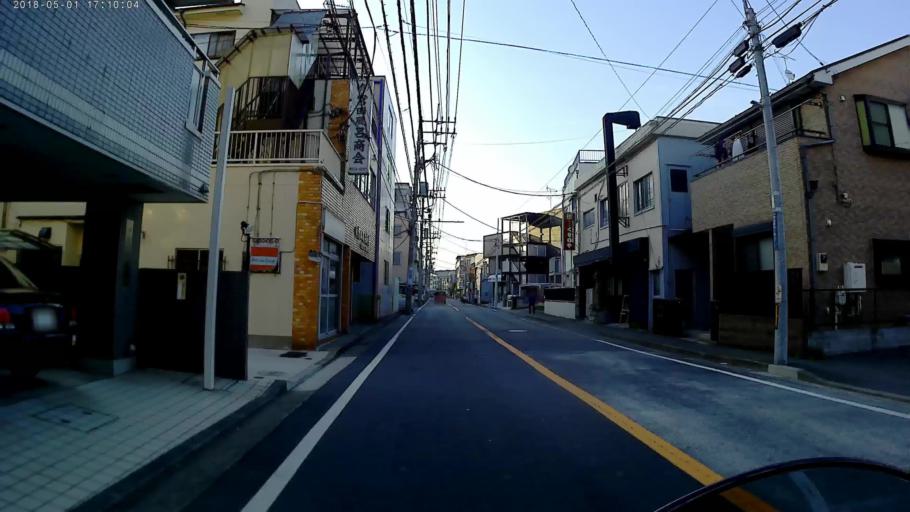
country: JP
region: Kanagawa
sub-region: Kawasaki-shi
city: Kawasaki
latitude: 35.5438
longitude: 139.6264
